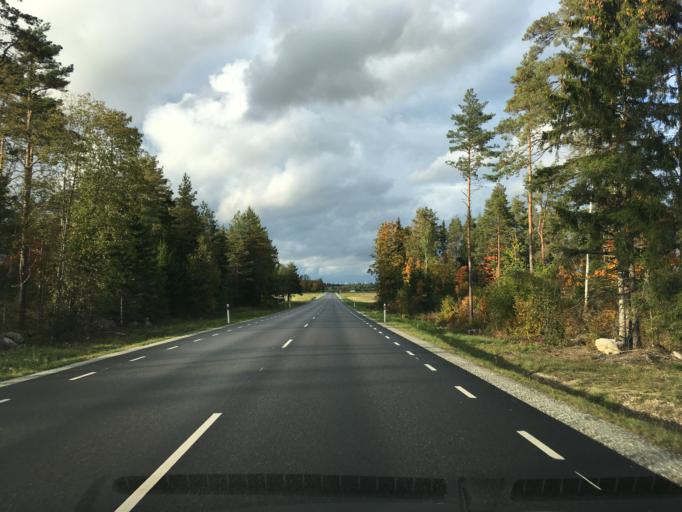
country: EE
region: Harju
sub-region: Paldiski linn
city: Paldiski
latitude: 59.2047
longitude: 24.0960
